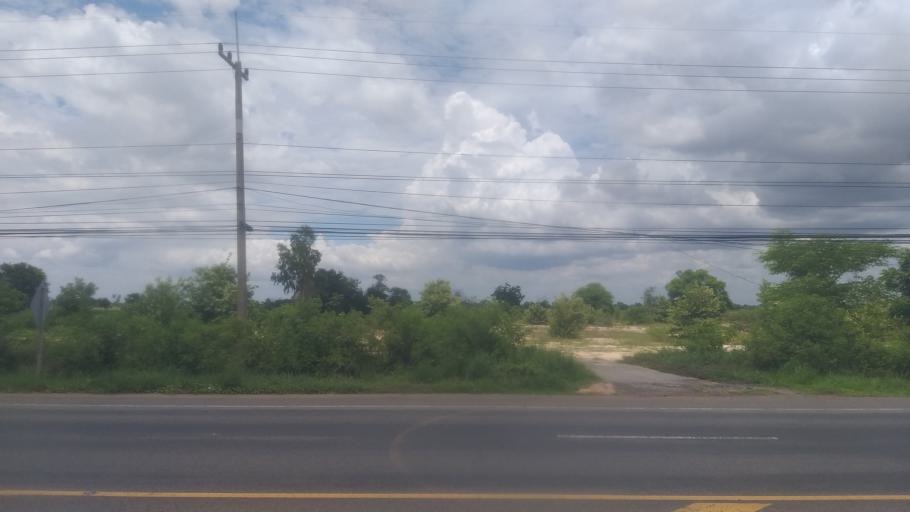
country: TH
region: Nakhon Ratchasima
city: Non Thai
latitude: 15.1015
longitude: 102.1046
